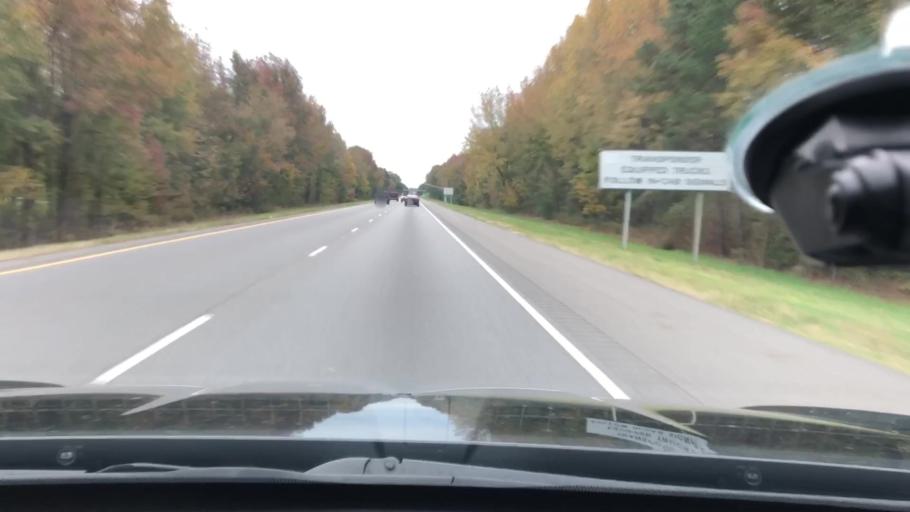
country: US
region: Arkansas
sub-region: Hempstead County
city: Hope
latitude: 33.6435
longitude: -93.6888
